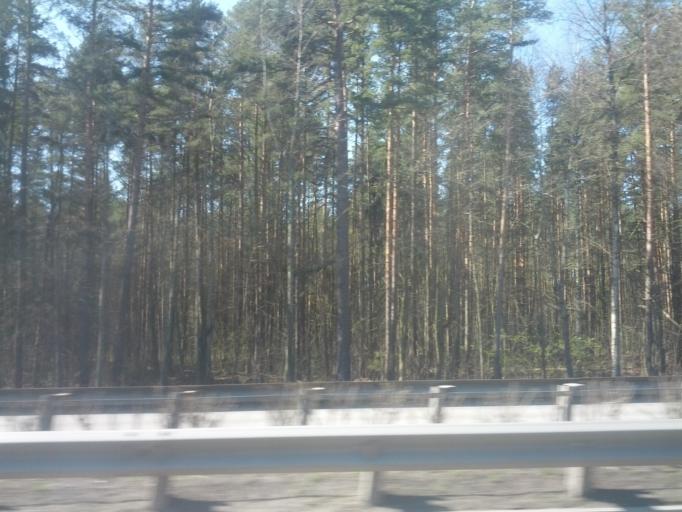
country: RU
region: St.-Petersburg
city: Tarkhovka
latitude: 60.0683
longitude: 29.9701
